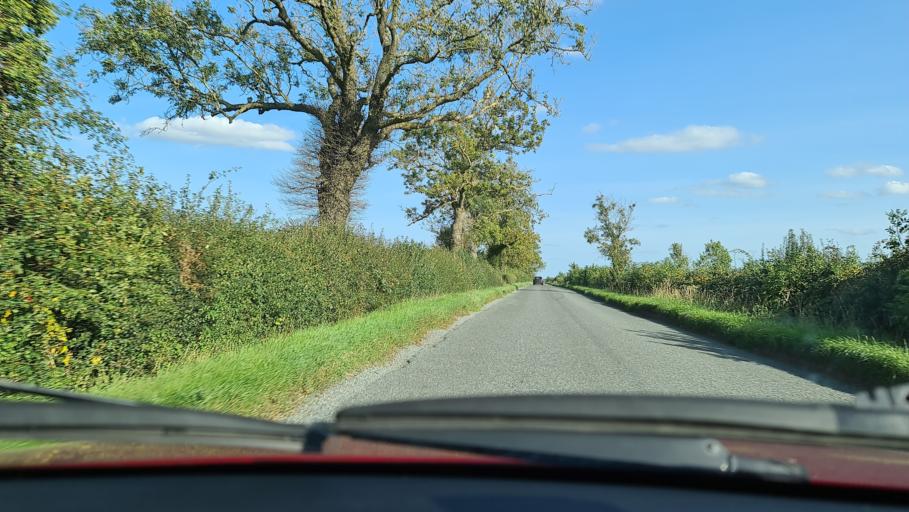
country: GB
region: England
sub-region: Northamptonshire
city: Brackley
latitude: 52.0204
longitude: -1.2155
